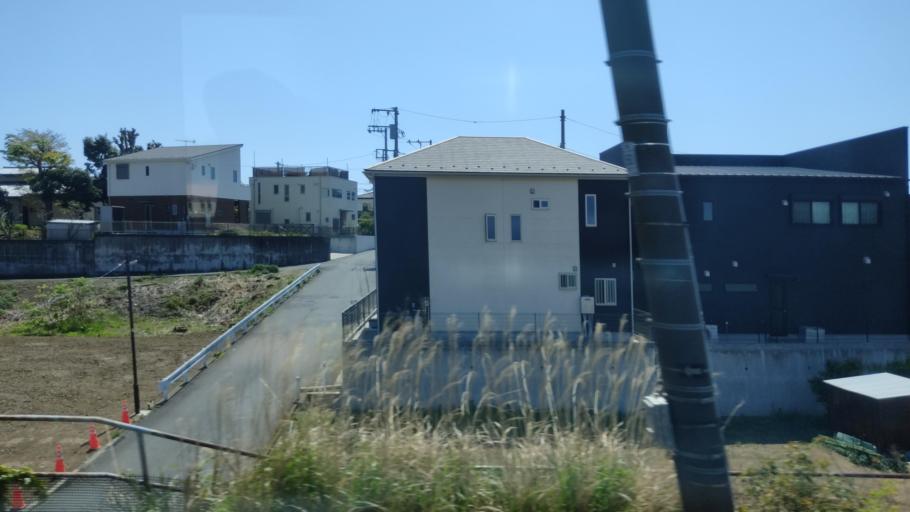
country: JP
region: Kanagawa
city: Oiso
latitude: 35.3062
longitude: 139.2842
